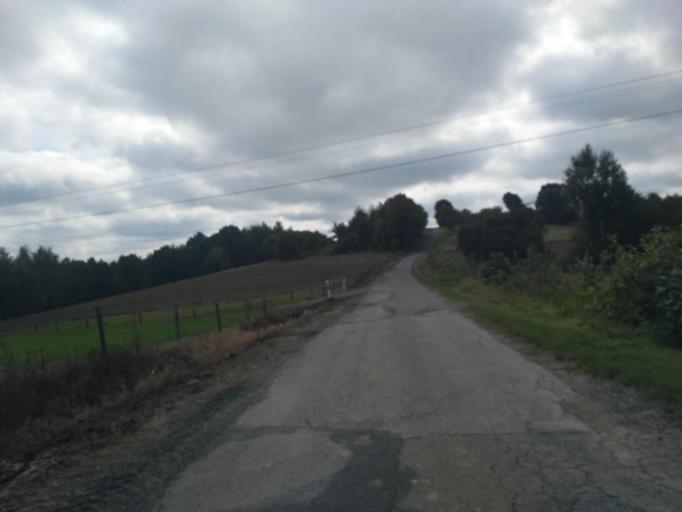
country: PL
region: Subcarpathian Voivodeship
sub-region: Powiat ropczycko-sedziszowski
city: Niedzwiada
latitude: 49.9479
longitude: 21.4623
